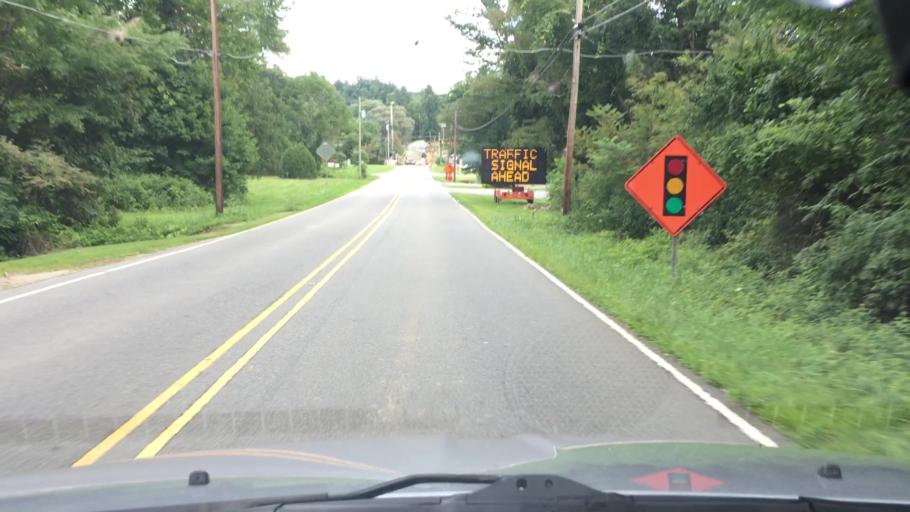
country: US
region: North Carolina
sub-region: Yancey County
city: Burnsville
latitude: 35.8538
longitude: -82.1996
